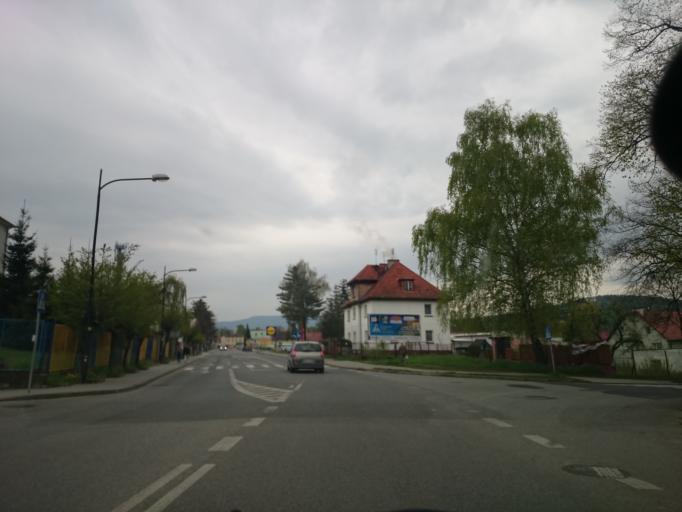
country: PL
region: Opole Voivodeship
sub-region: Powiat nyski
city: Glucholazy
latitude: 50.3204
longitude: 17.3881
